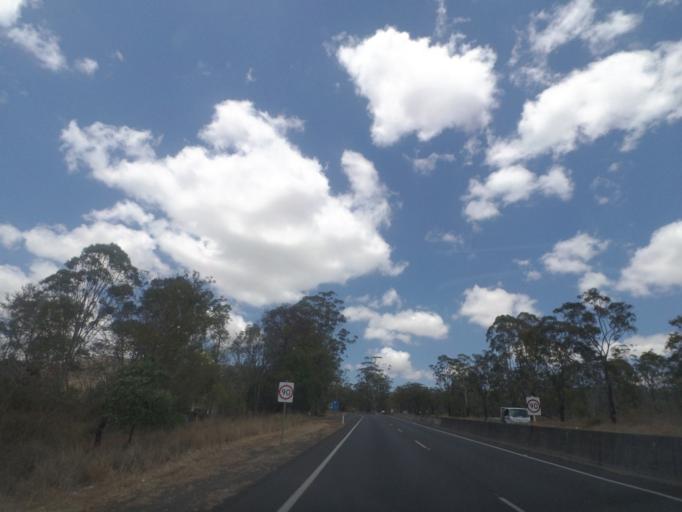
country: AU
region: Queensland
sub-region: Toowoomba
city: East Toowoomba
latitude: -27.5644
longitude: 152.0008
